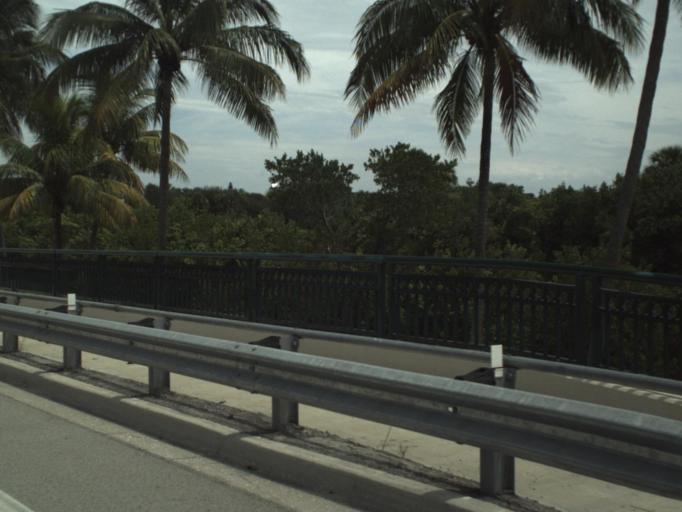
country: US
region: Florida
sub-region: Palm Beach County
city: Jupiter
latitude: 26.9379
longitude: -80.0830
